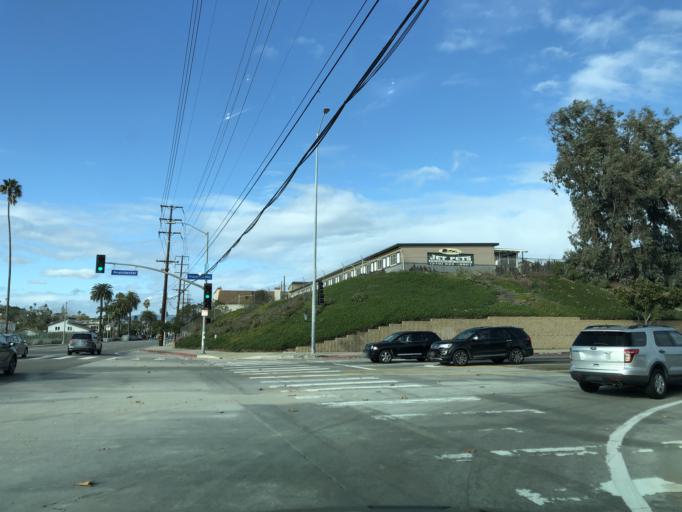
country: US
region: California
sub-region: Los Angeles County
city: Marina del Rey
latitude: 33.9515
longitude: -118.4389
